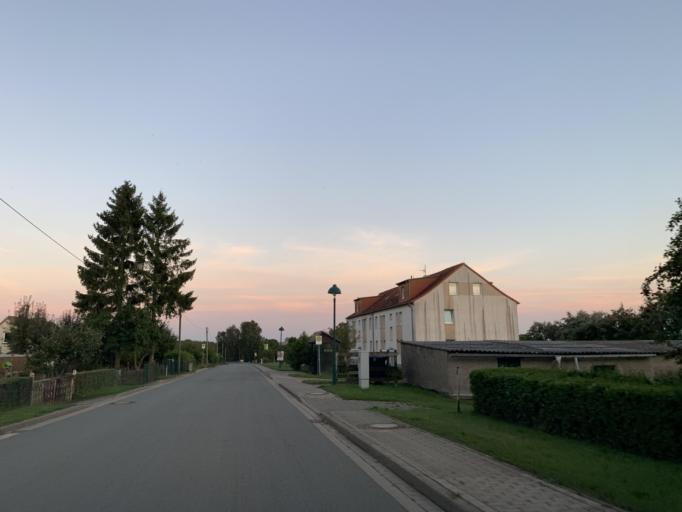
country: DE
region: Mecklenburg-Vorpommern
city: Blankensee
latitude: 53.4429
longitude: 13.2993
